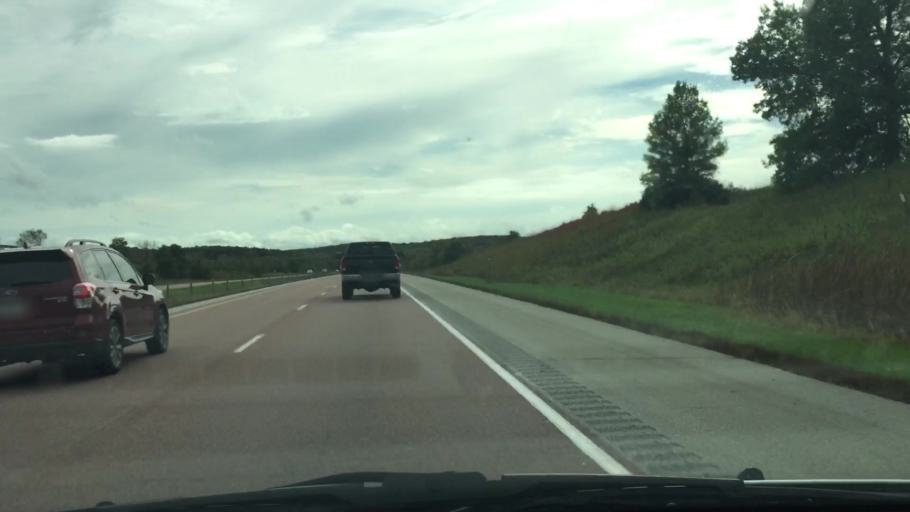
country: US
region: Iowa
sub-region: Clarke County
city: Osceola
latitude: 41.2101
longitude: -93.7852
